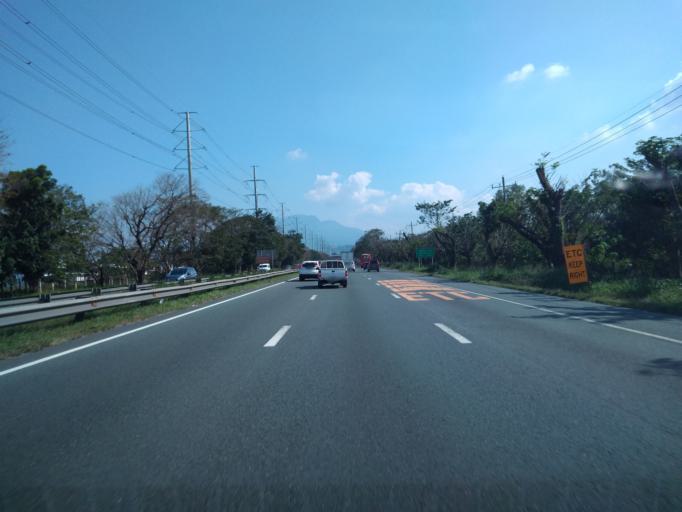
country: PH
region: Calabarzon
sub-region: Province of Laguna
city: Prinza
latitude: 14.2275
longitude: 121.1200
